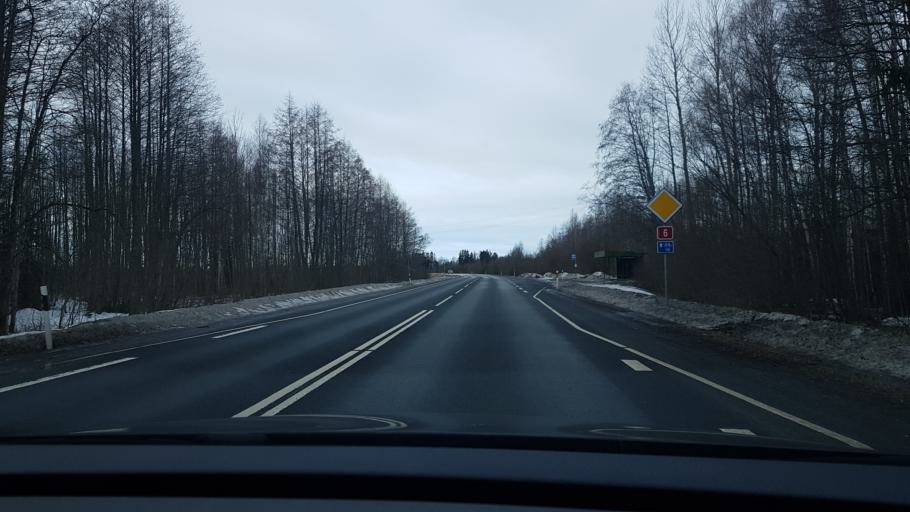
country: EE
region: Paernumaa
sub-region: Paikuse vald
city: Paikuse
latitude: 58.2596
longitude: 24.6712
